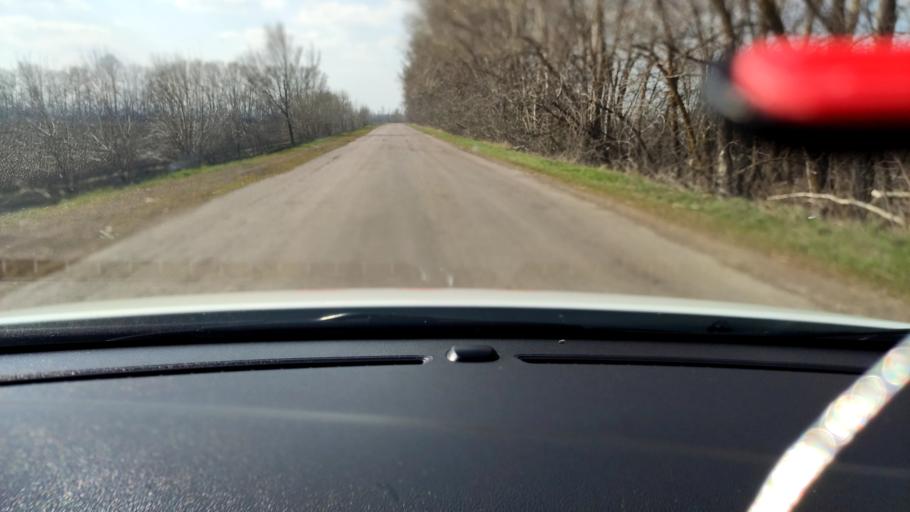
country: RU
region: Voronezj
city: Uryv-Pokrovka
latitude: 51.1298
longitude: 39.1039
